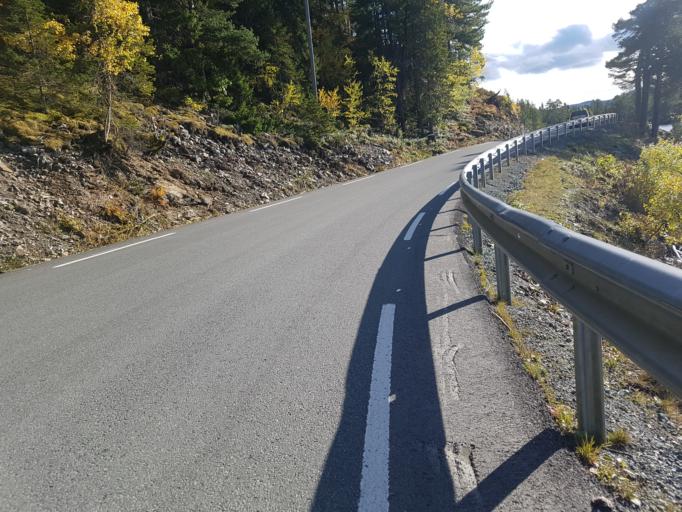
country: NO
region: Sor-Trondelag
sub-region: Malvik
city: Malvik
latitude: 63.3751
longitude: 10.6106
